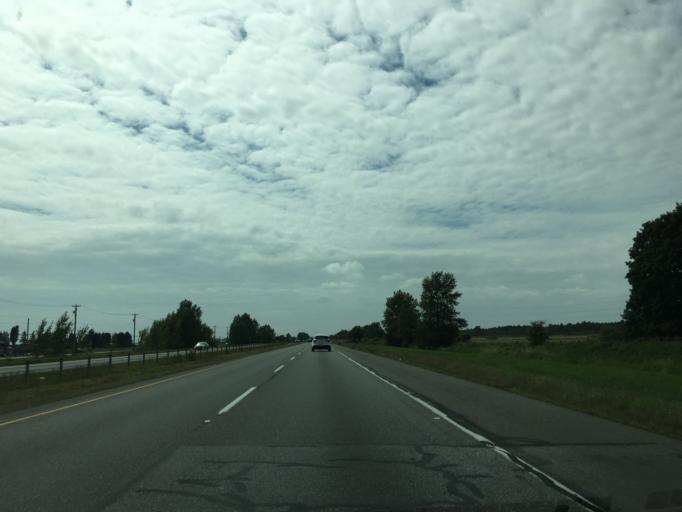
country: CA
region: British Columbia
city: Delta
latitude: 49.0905
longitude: -122.9710
